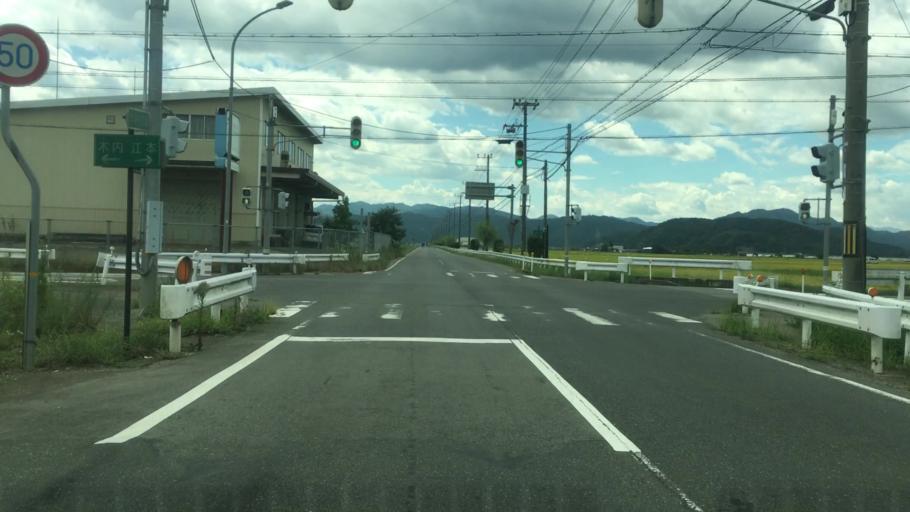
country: JP
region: Hyogo
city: Toyooka
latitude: 35.5249
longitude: 134.8398
